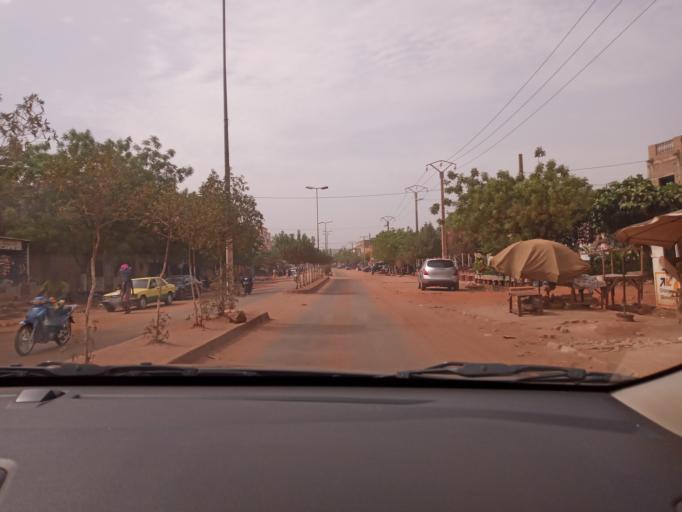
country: ML
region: Bamako
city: Bamako
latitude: 12.6705
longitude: -7.9242
